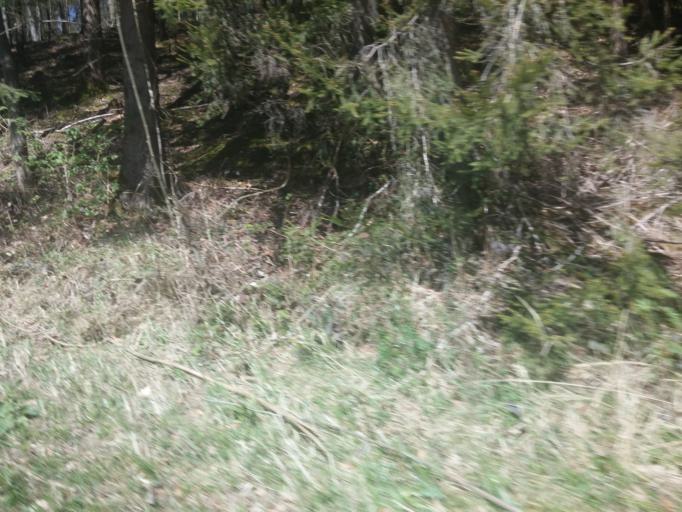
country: DE
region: Baden-Wuerttemberg
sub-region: Tuebingen Region
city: Aitrach
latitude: 47.9342
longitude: 10.1155
